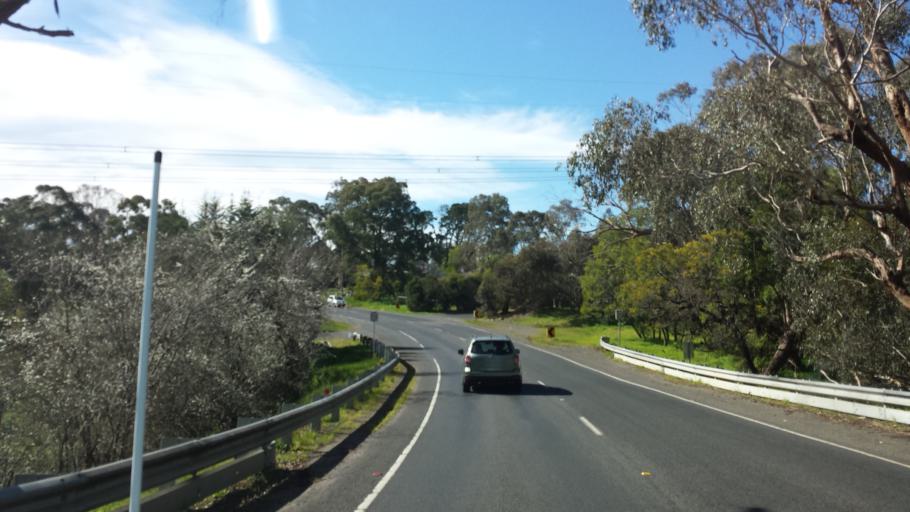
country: AU
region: Victoria
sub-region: Manningham
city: Warrandyte
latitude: -37.7649
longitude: 145.2311
